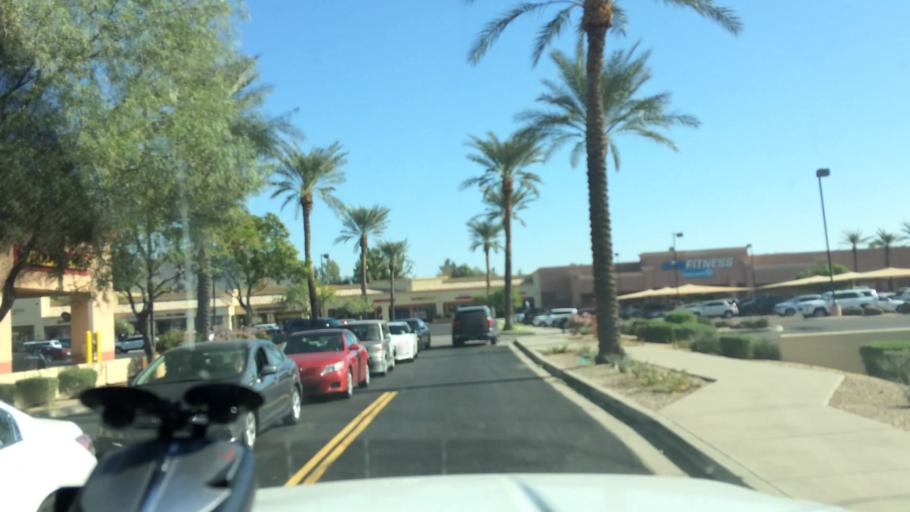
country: US
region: Arizona
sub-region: Maricopa County
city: Peoria
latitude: 33.6705
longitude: -112.1864
